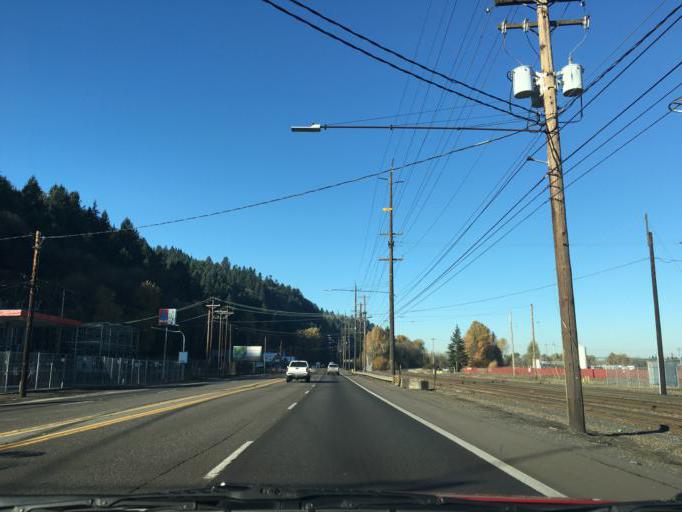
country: US
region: Oregon
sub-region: Washington County
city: West Haven
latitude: 45.5658
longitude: -122.7487
